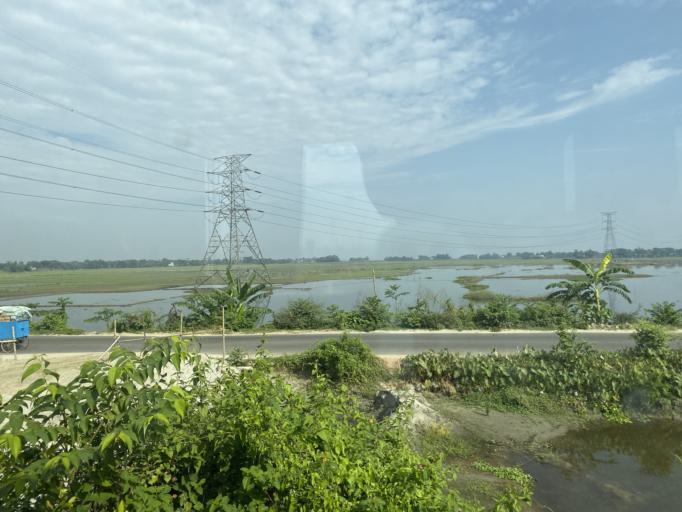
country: IN
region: Tripura
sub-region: West Tripura
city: Agartala
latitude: 23.8799
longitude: 91.1955
